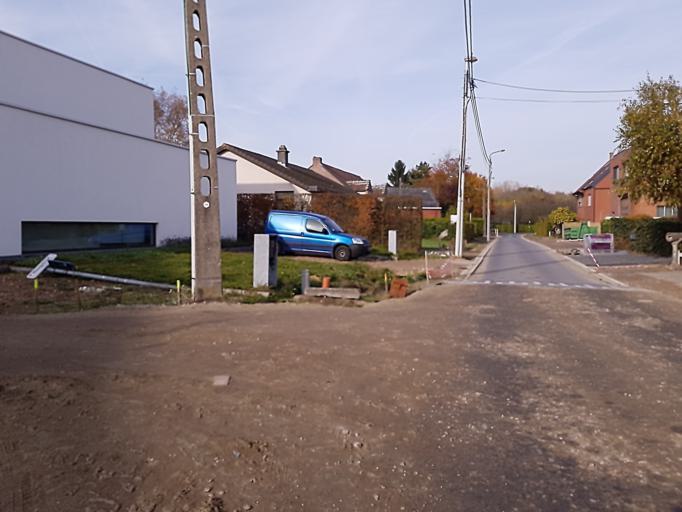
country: BE
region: Flanders
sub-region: Provincie Antwerpen
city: Sint-Katelijne-Waver
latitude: 51.0542
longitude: 4.5735
